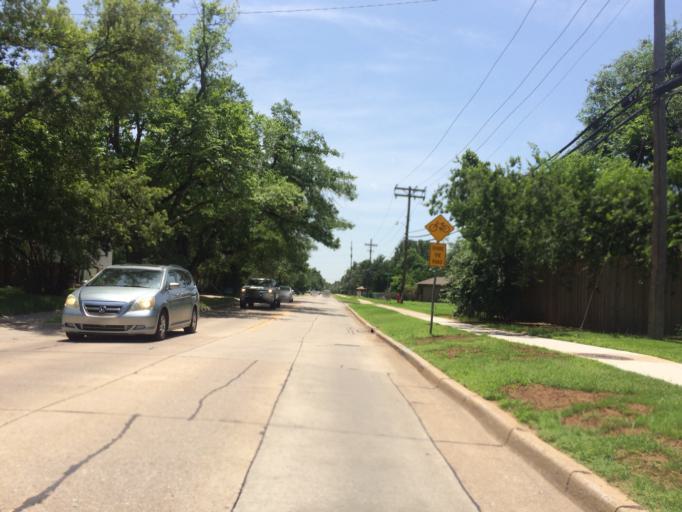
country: US
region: Oklahoma
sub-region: Cleveland County
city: Norman
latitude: 35.2168
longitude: -97.4590
